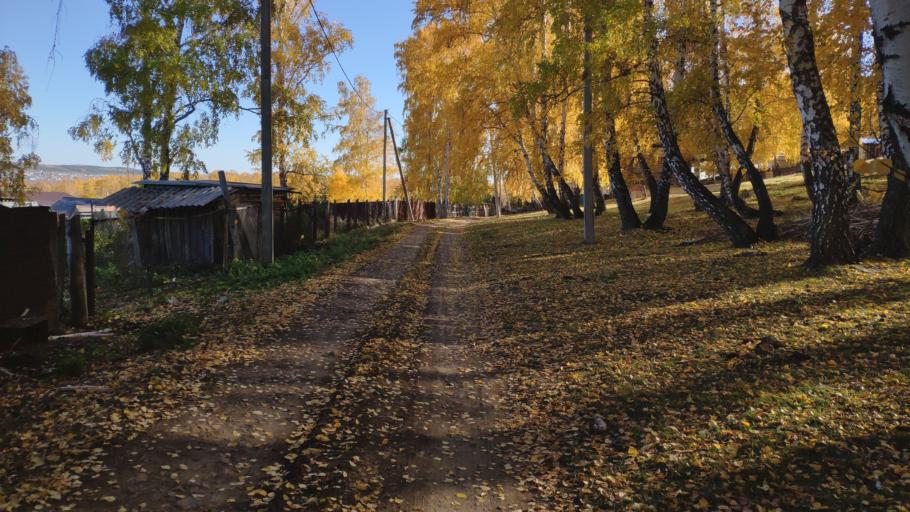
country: RU
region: Bashkortostan
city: Abzakovo
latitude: 53.3447
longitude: 58.5026
